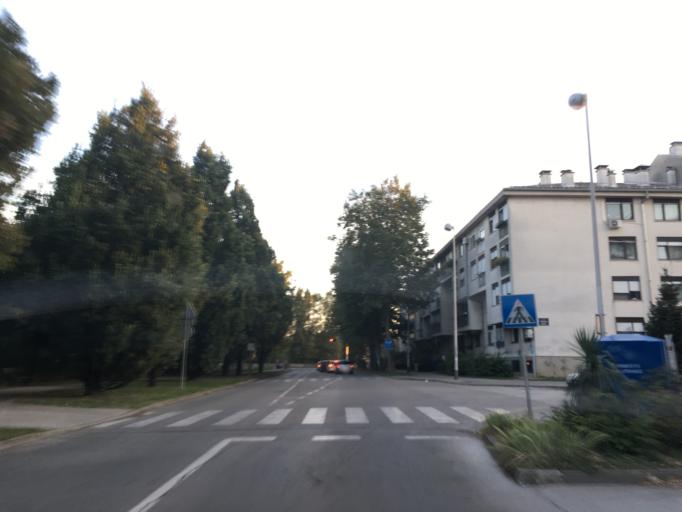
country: HR
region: Grad Zagreb
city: Jankomir
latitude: 45.7853
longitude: 15.9412
